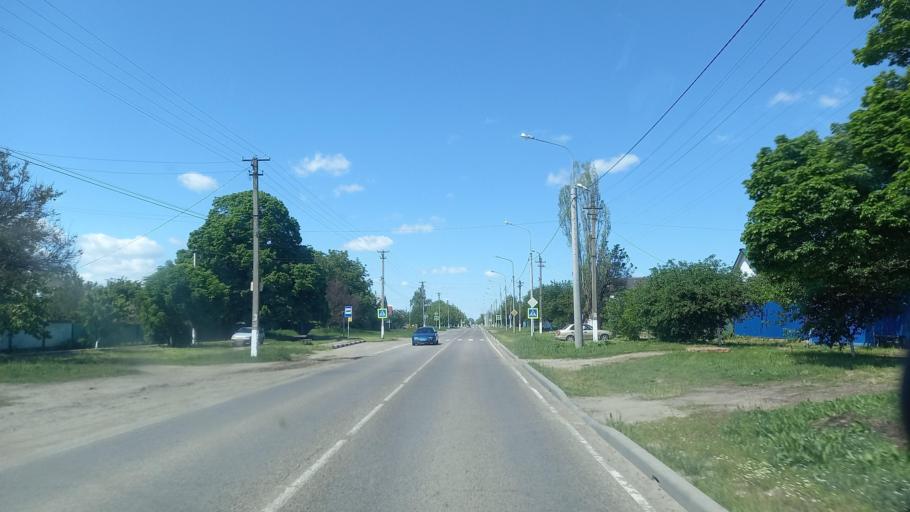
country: RU
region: Krasnodarskiy
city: Novoukrainskoye
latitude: 45.3801
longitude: 40.5369
